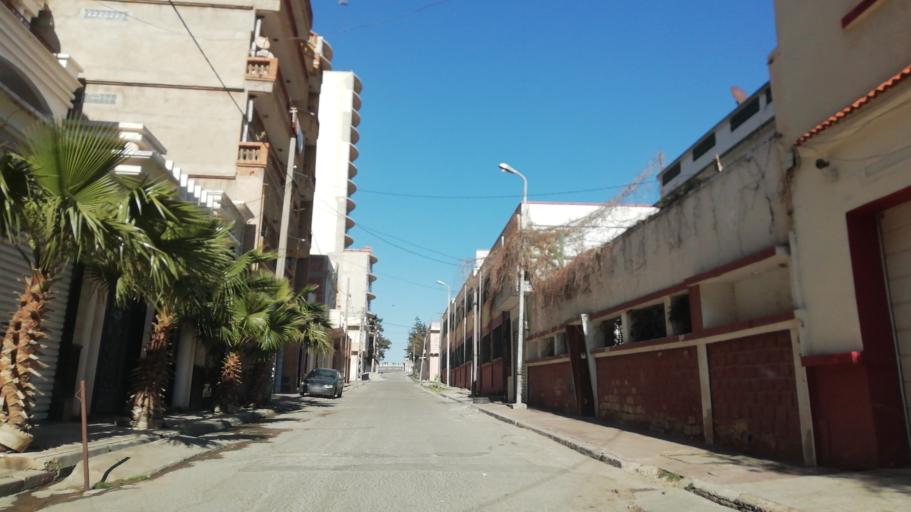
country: DZ
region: Oran
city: Oran
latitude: 35.7124
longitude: -0.6206
